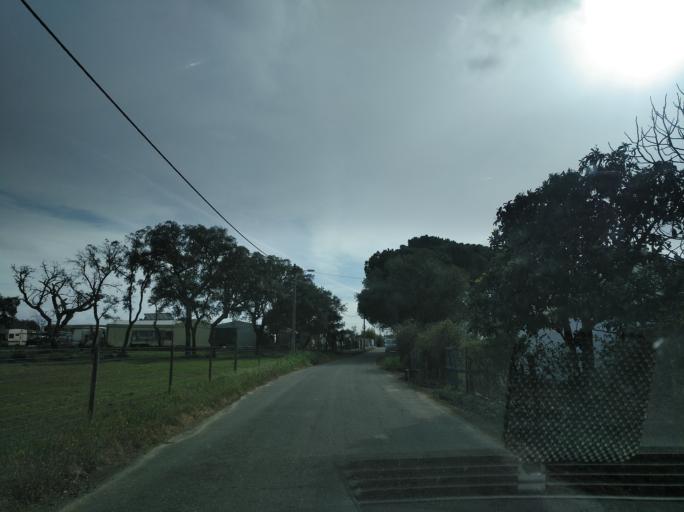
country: PT
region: Setubal
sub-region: Grandola
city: Grandola
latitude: 38.2006
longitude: -8.5455
